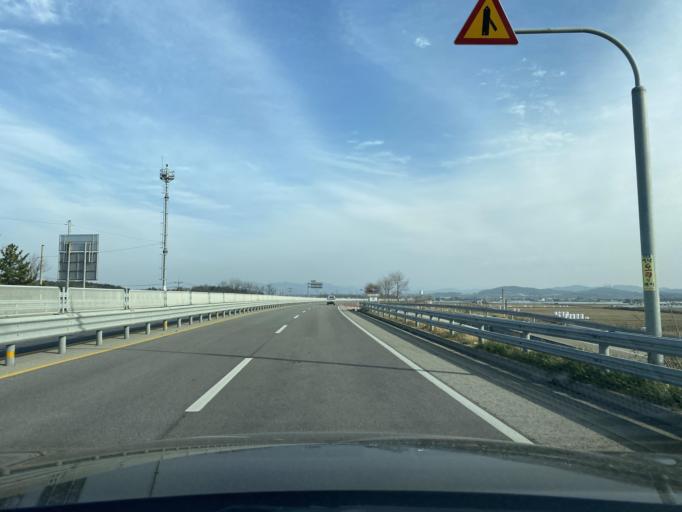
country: KR
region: Chungcheongnam-do
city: Hongsung
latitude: 36.6909
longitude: 126.6968
